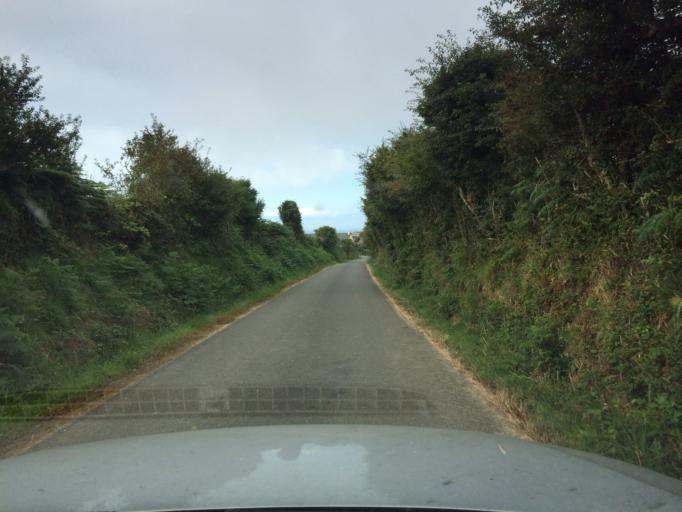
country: FR
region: Lower Normandy
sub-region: Departement de la Manche
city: Beaumont-Hague
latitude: 49.6795
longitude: -1.9135
